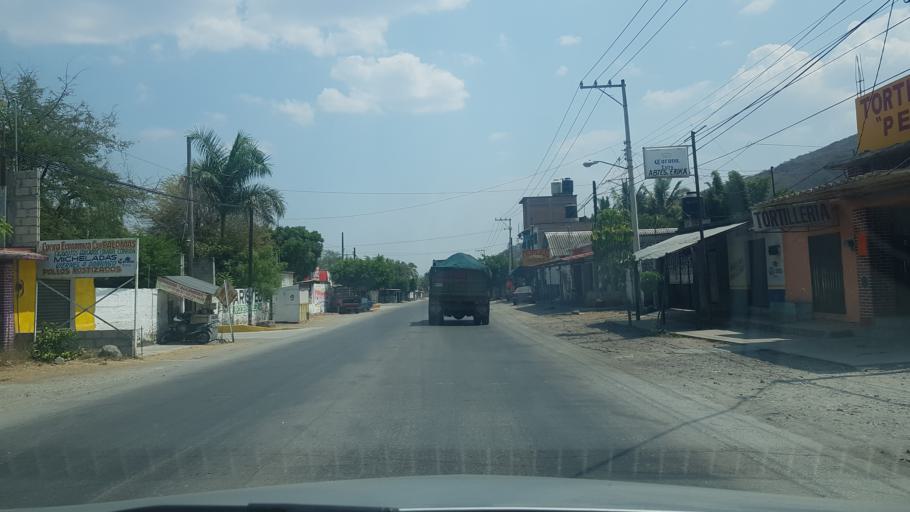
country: MX
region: Morelos
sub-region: Tlaltizapan de Zapata
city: Colonia Palo Prieto (Chipitongo)
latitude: 18.7187
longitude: -99.1203
